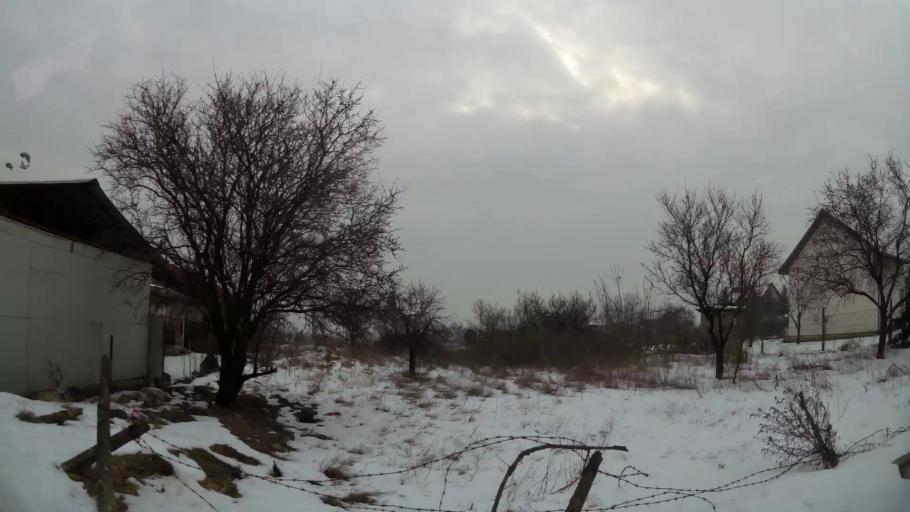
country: MK
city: Kondovo
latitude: 42.0426
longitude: 21.3420
